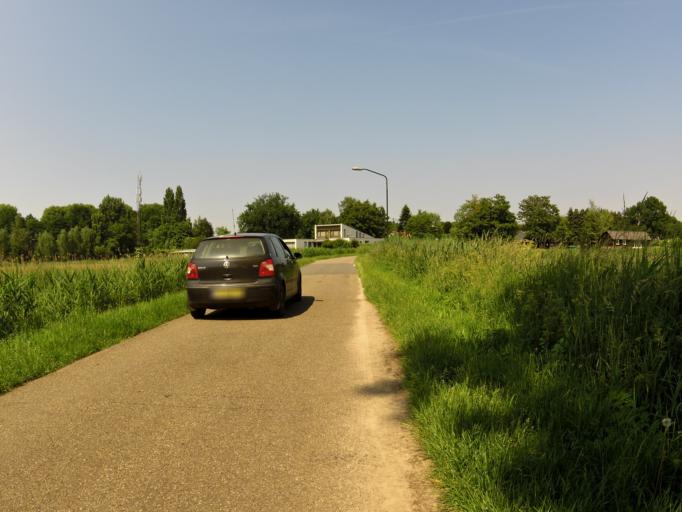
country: NL
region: North Brabant
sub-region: Gemeente Sint-Michielsgestel
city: Sint-Michielsgestel
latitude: 51.6356
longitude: 5.3575
